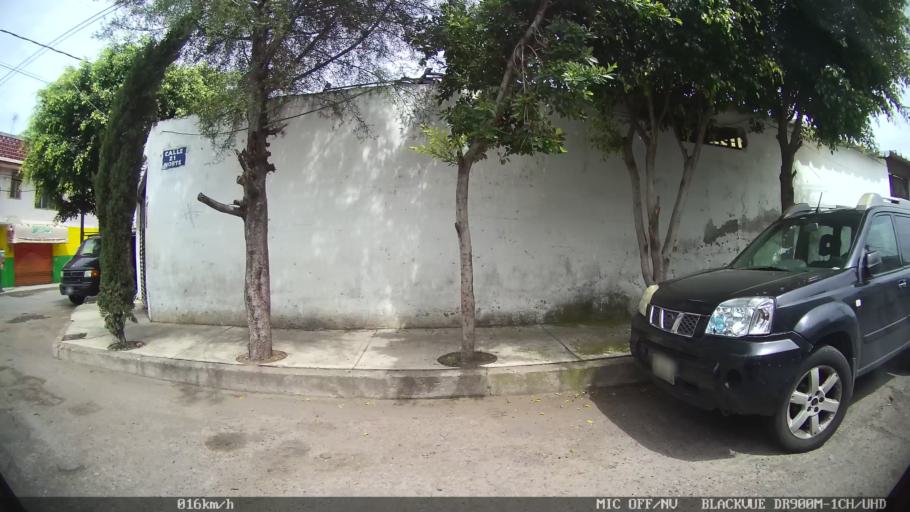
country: MX
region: Puebla
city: Puebla
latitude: 19.0698
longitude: -98.1992
